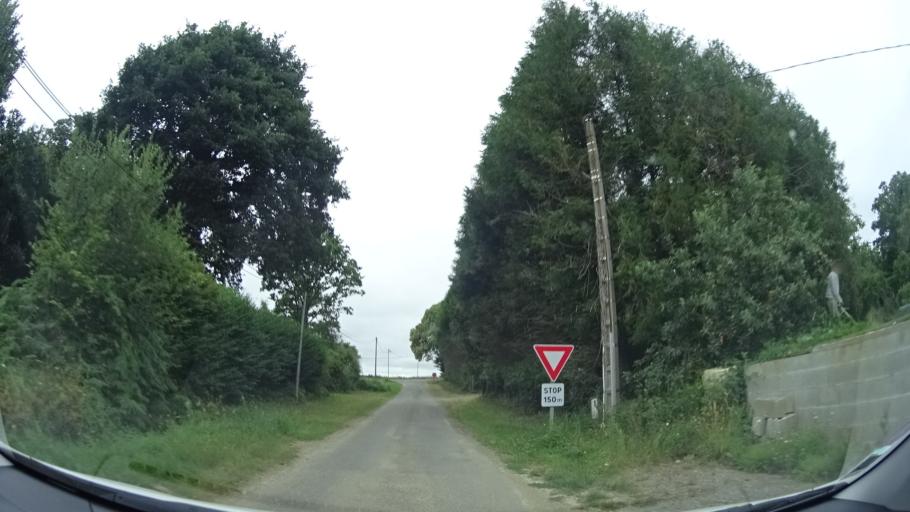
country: FR
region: Brittany
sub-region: Departement des Cotes-d'Armor
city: Evran
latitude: 48.3413
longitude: -1.9478
